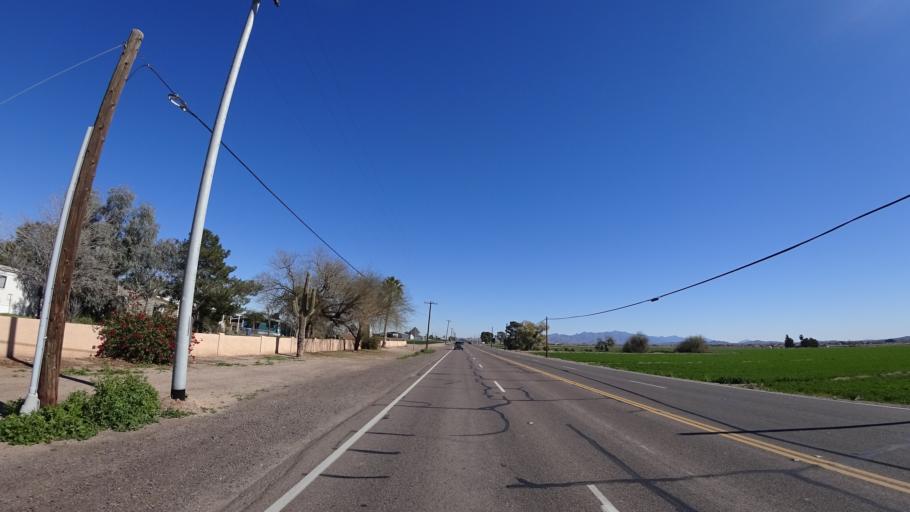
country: US
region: Arizona
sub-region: Maricopa County
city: Buckeye
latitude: 33.3776
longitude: -112.5600
